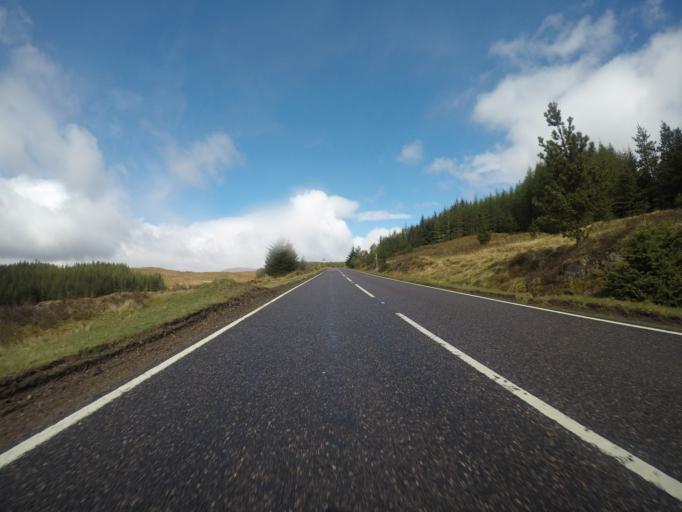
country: GB
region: Scotland
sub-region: Highland
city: Spean Bridge
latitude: 57.0908
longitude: -4.9836
